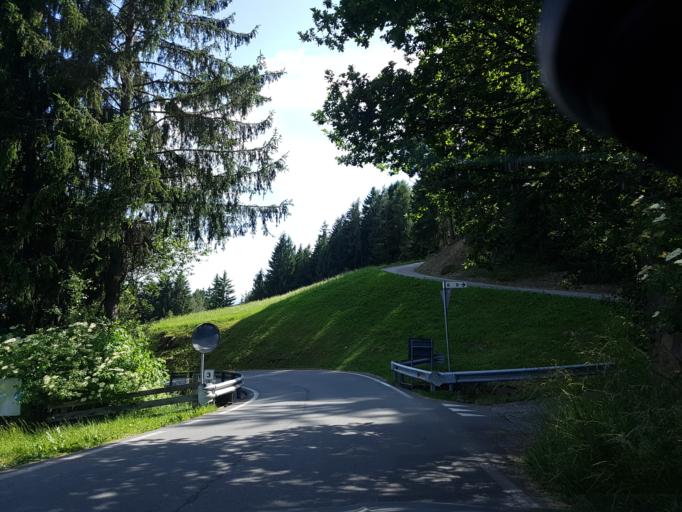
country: IT
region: Trentino-Alto Adige
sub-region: Bolzano
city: Villandro - Villanders
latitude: 46.6327
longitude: 11.5259
